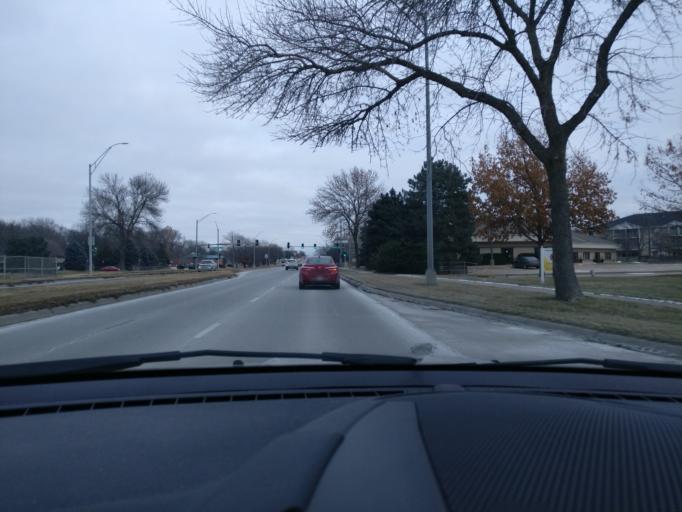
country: US
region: Nebraska
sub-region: Lancaster County
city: Lincoln
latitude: 40.8134
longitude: -96.6177
